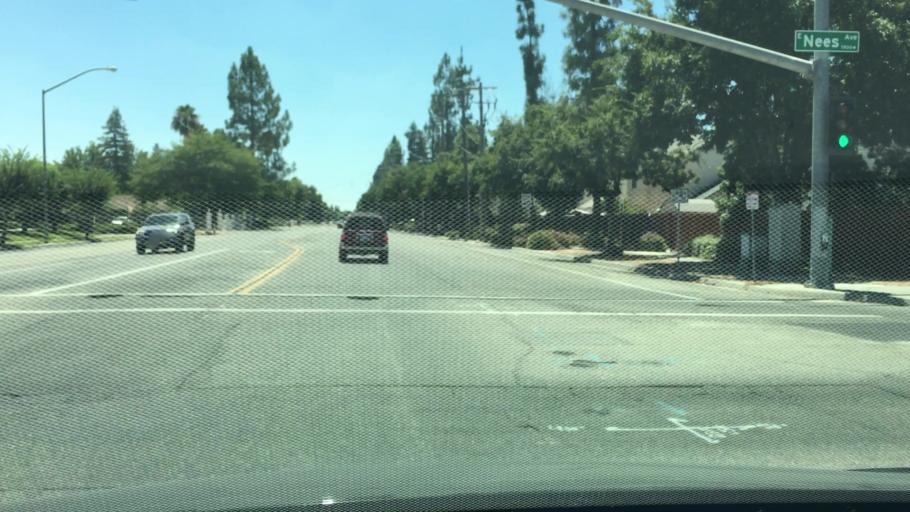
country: US
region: California
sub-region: Fresno County
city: Clovis
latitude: 36.8520
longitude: -119.7478
